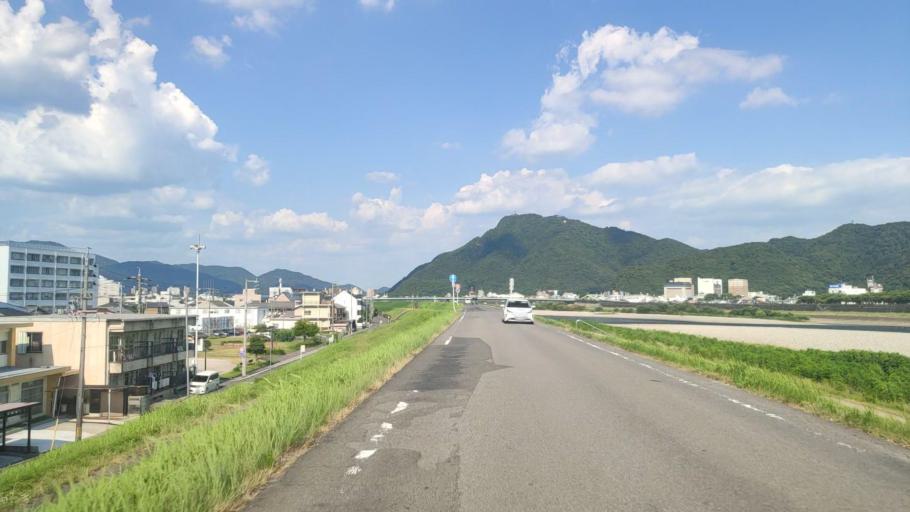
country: JP
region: Gifu
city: Gifu-shi
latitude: 35.4322
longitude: 136.7543
